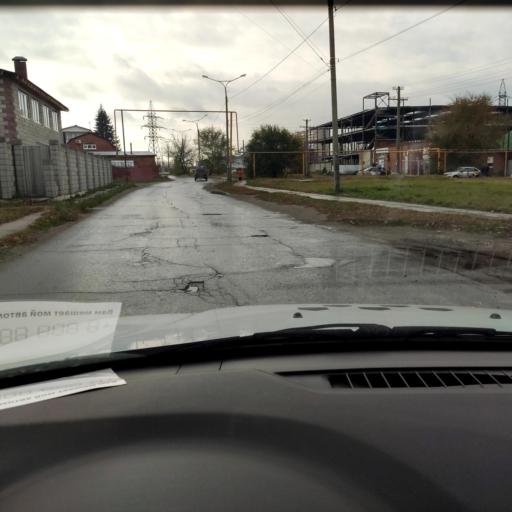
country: RU
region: Samara
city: Tol'yatti
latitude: 53.5379
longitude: 49.3969
